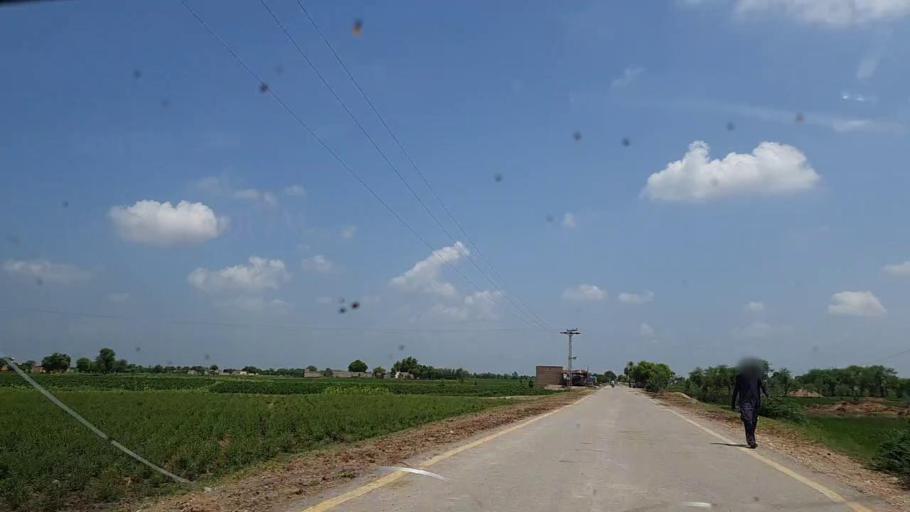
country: PK
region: Sindh
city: Tharu Shah
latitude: 26.9835
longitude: 68.0803
